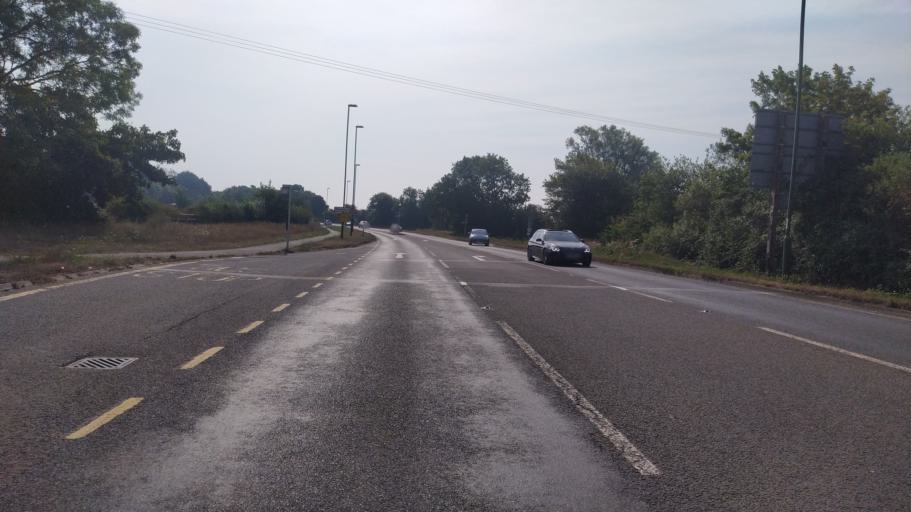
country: GB
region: England
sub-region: West Sussex
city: Boxgrove
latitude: 50.8242
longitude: -0.7327
